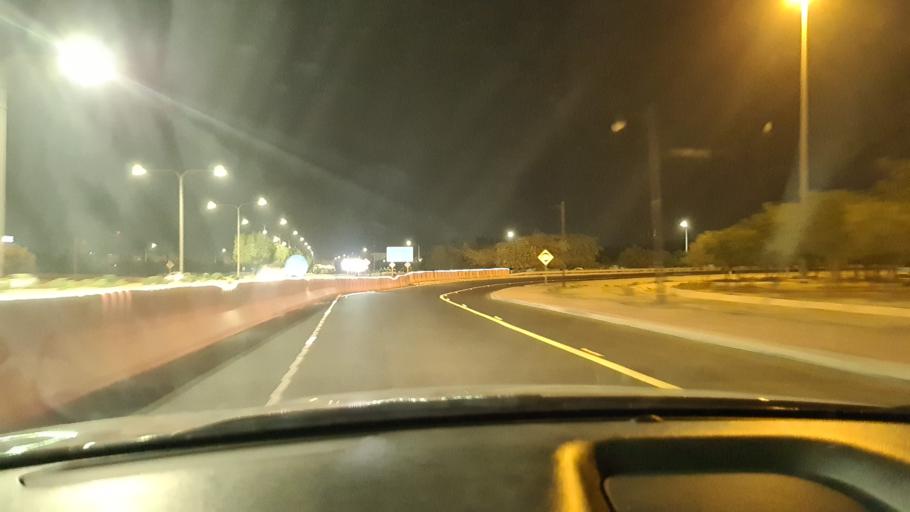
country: SA
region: Eastern Province
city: Al Jubayl
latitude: 27.1374
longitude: 49.5579
